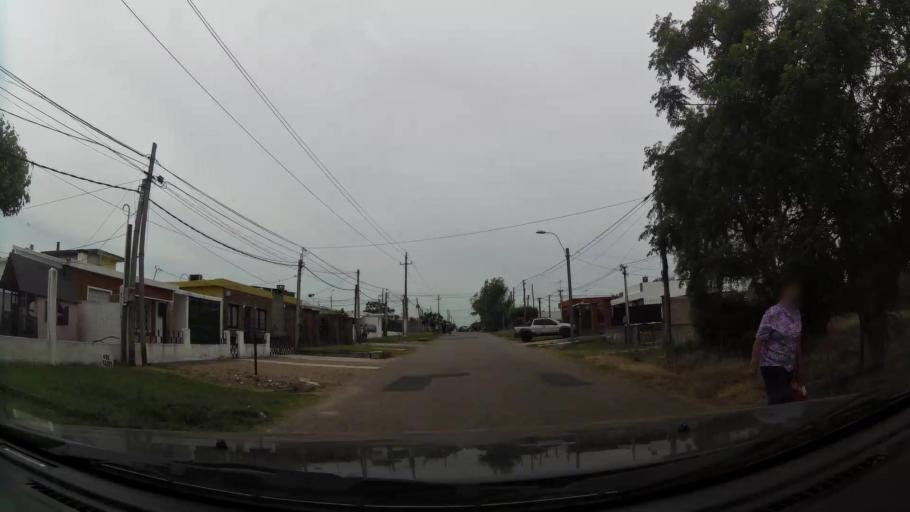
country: UY
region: Canelones
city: Las Piedras
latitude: -34.7395
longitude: -56.2294
